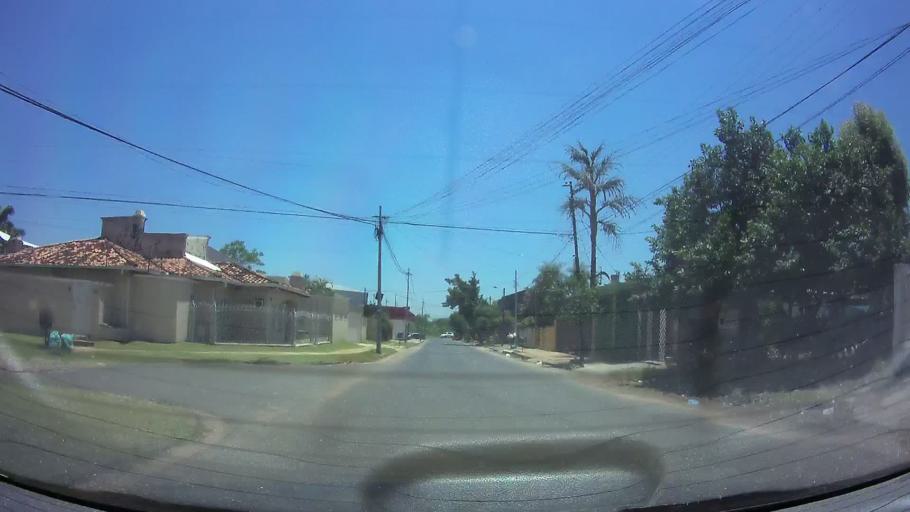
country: PY
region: Central
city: Fernando de la Mora
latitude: -25.2819
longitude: -57.5345
